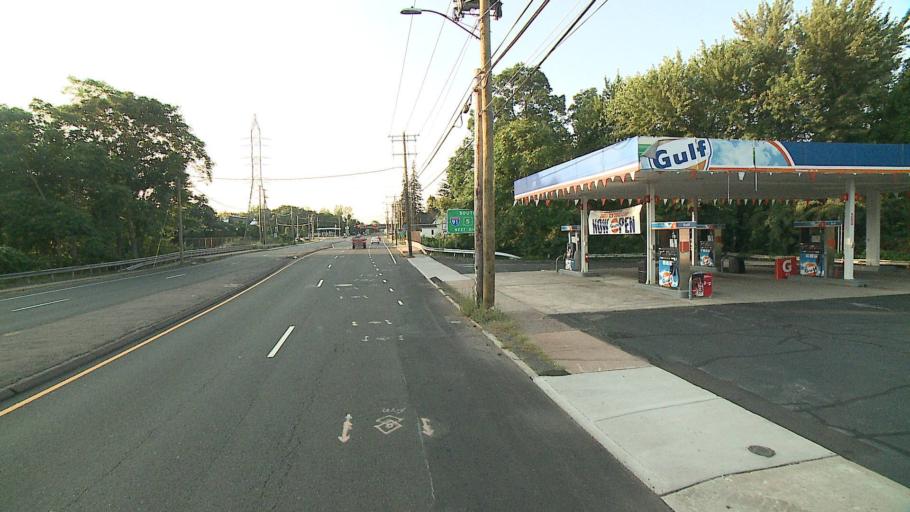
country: US
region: Connecticut
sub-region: Hartford County
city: Hartford
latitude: 41.7619
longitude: -72.6458
